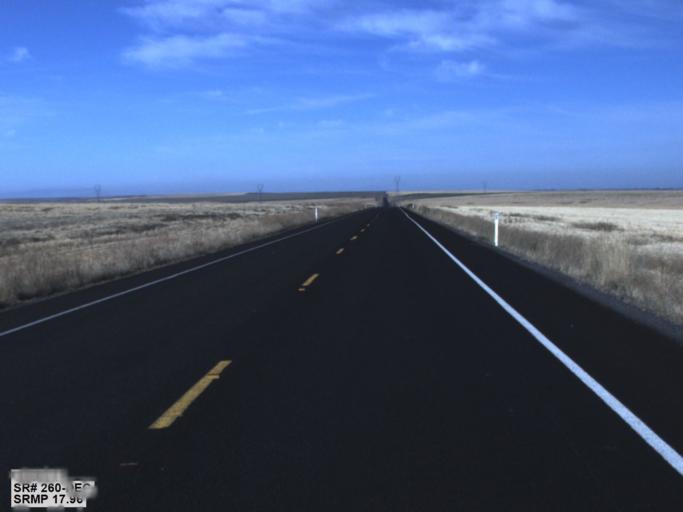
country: US
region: Washington
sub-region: Franklin County
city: Connell
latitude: 46.6203
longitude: -118.6801
